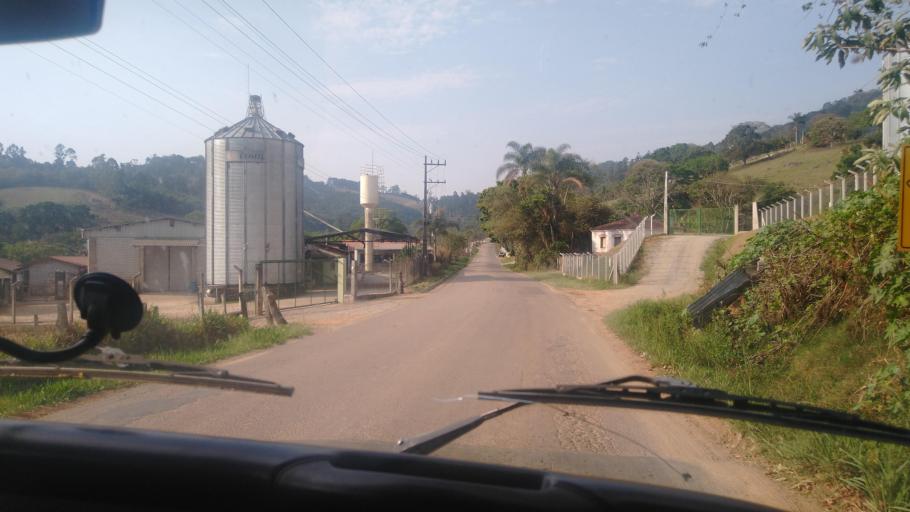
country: BR
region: Minas Gerais
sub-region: Extrema
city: Extrema
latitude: -22.7824
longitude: -46.4424
